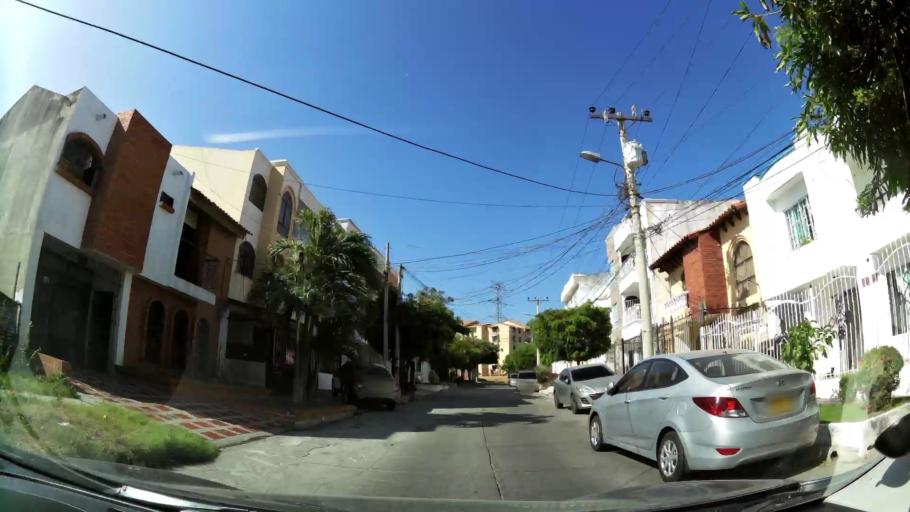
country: CO
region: Atlantico
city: Barranquilla
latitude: 11.0235
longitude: -74.8104
